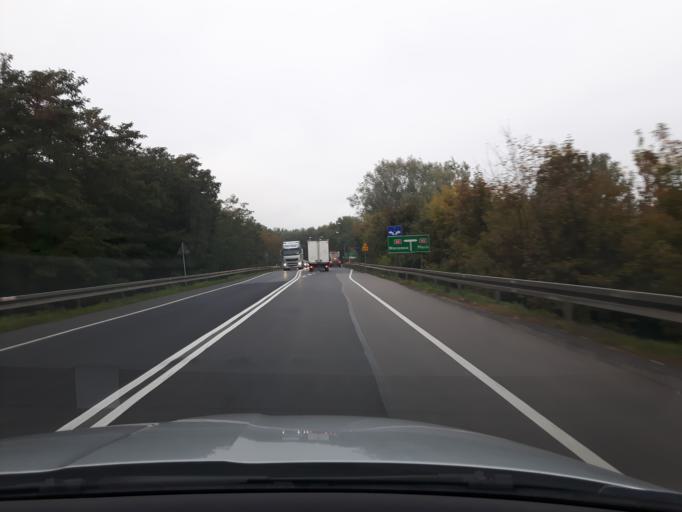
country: PL
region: Masovian Voivodeship
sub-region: Powiat nowodworski
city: Nowy Dwor Mazowiecki
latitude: 52.4284
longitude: 20.6978
